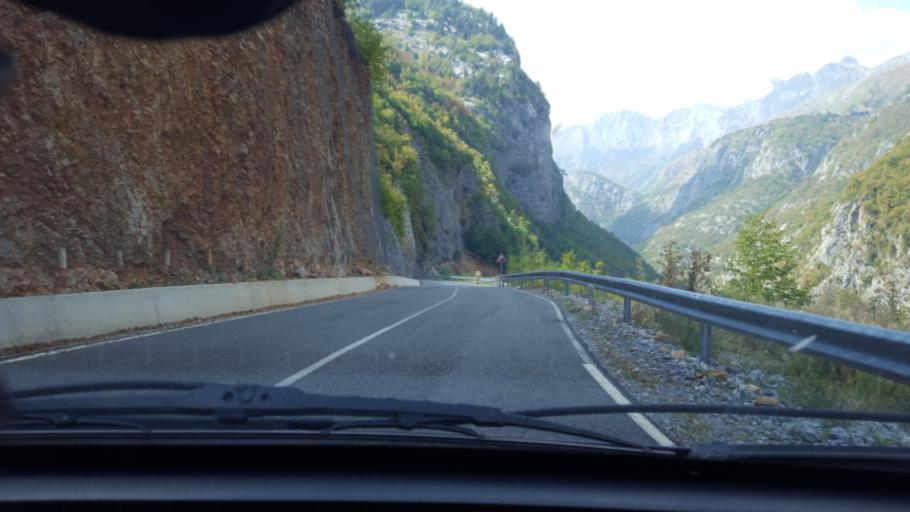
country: ME
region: Andrijevica
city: Andrijevica
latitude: 42.5333
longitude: 19.6727
